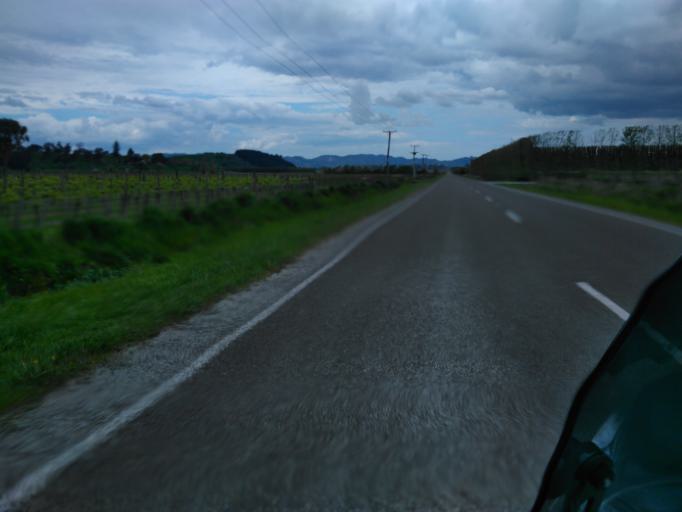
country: NZ
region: Gisborne
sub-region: Gisborne District
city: Gisborne
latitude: -38.6443
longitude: 177.8687
